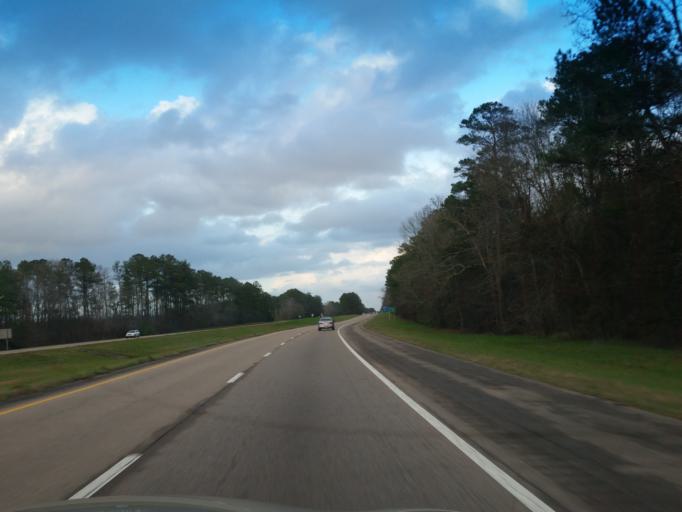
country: US
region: Mississippi
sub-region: Clarke County
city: Stonewall
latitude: 32.0481
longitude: -88.9171
